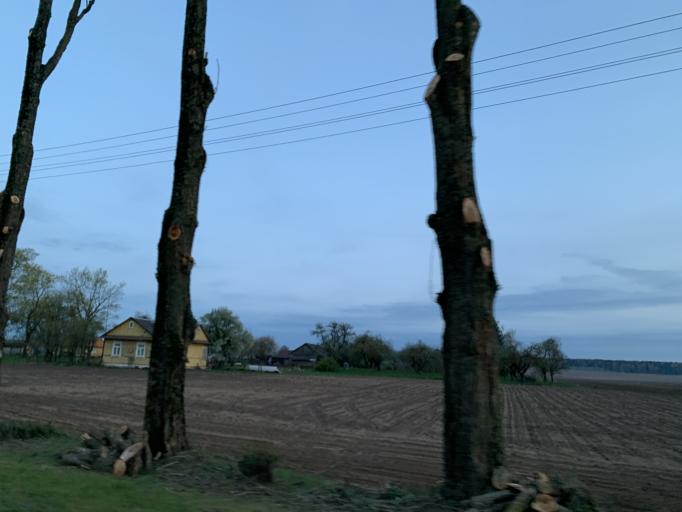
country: BY
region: Minsk
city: Snow
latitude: 53.1673
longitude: 26.5164
